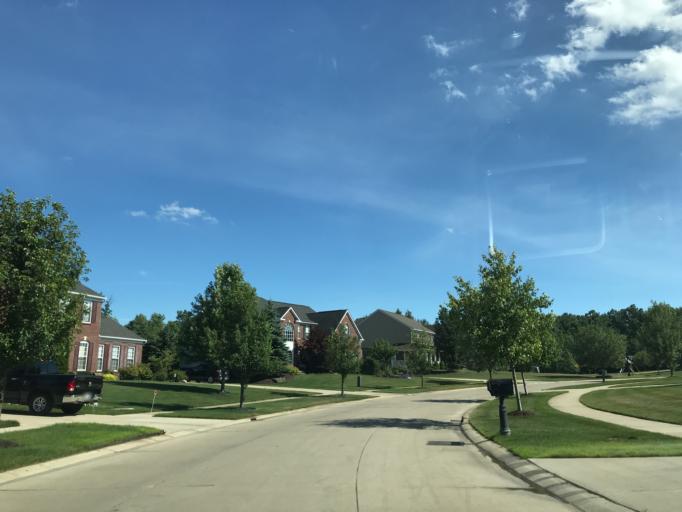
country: US
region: Michigan
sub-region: Oakland County
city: Wixom
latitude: 42.4604
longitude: -83.5667
